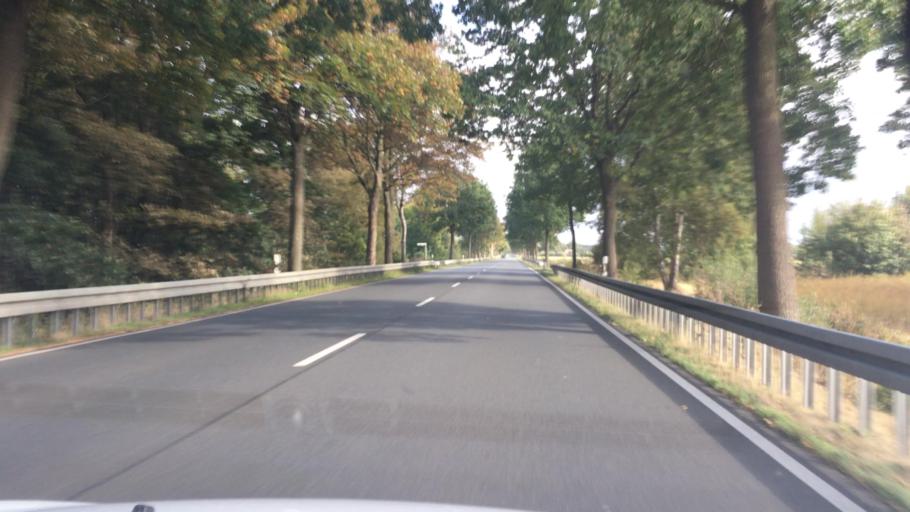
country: DE
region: Lower Saxony
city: Barver
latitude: 52.6104
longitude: 8.5513
